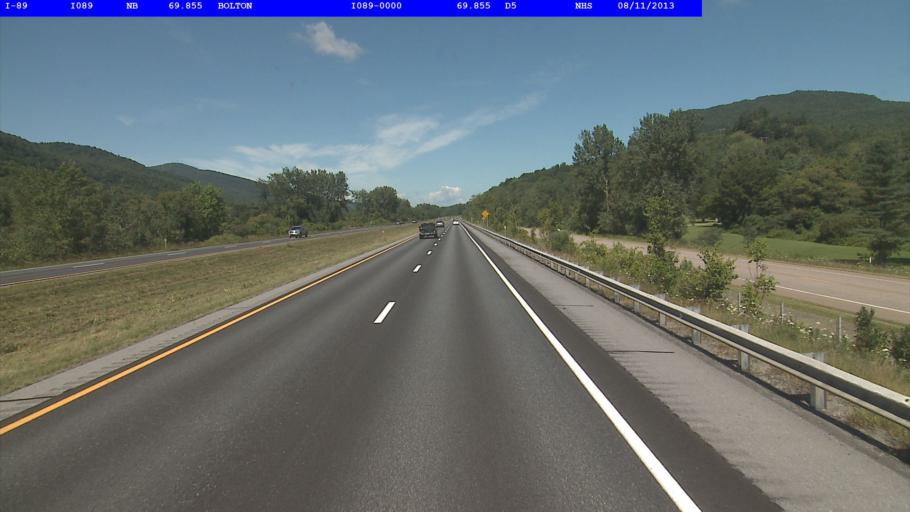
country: US
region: Vermont
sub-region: Washington County
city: Waterbury
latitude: 44.3692
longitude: -72.8653
